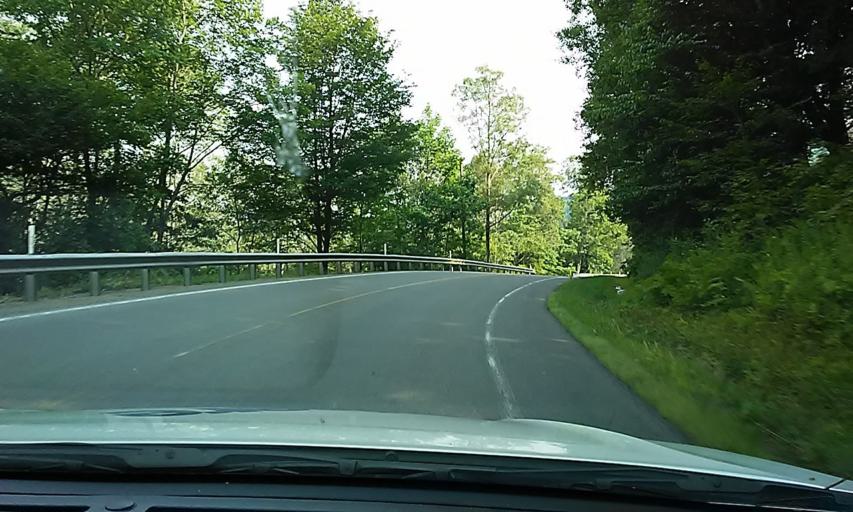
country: US
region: Pennsylvania
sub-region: Potter County
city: Galeton
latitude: 41.8070
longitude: -77.7772
